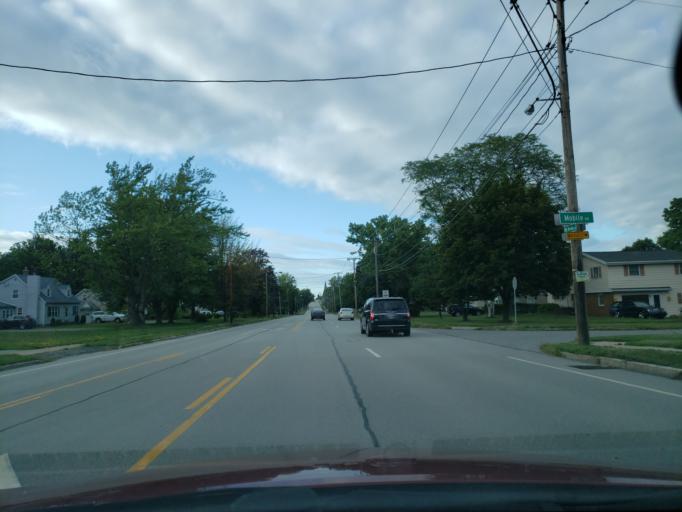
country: US
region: New York
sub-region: Monroe County
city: Greece
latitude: 43.2448
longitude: -77.6591
